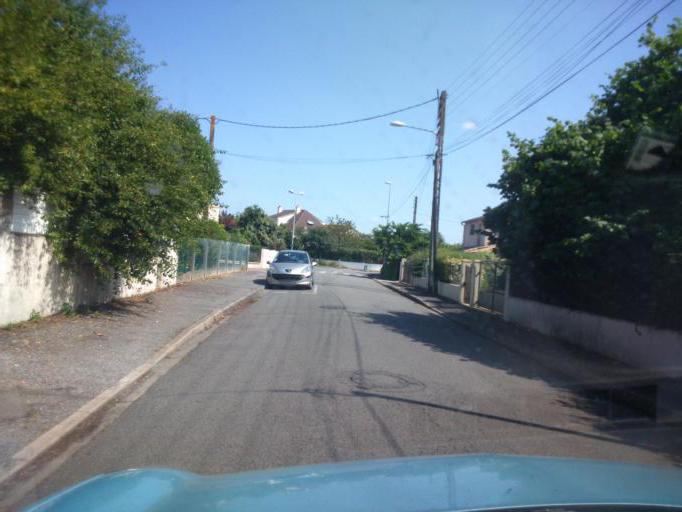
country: FR
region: Pays de la Loire
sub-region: Departement de la Loire-Atlantique
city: Saint-Sebastien-sur-Loire
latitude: 47.2000
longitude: -1.5153
